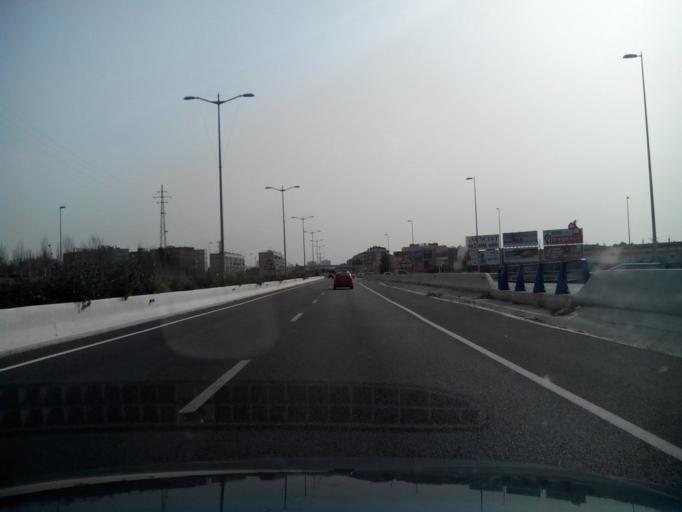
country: ES
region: Catalonia
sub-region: Provincia de Tarragona
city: Constanti
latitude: 41.1263
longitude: 1.2070
